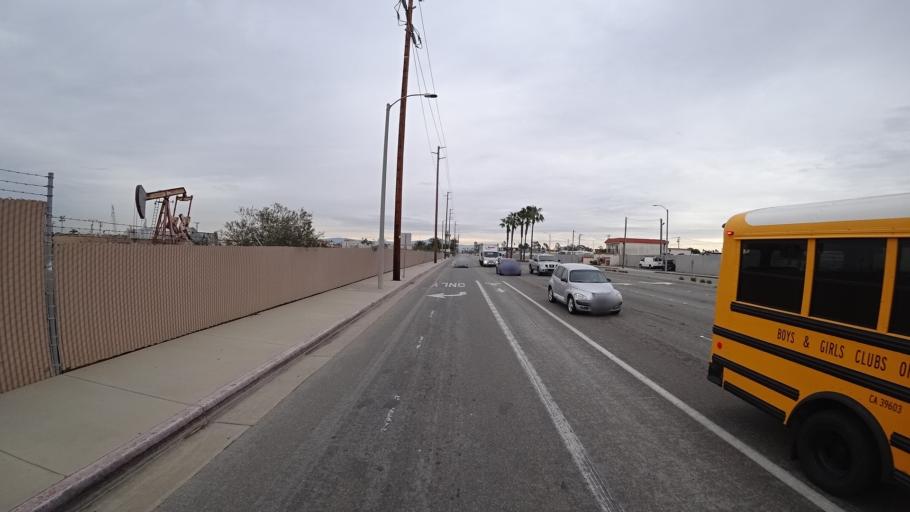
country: US
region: California
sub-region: Orange County
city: Huntington Beach
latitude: 33.6866
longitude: -118.0057
